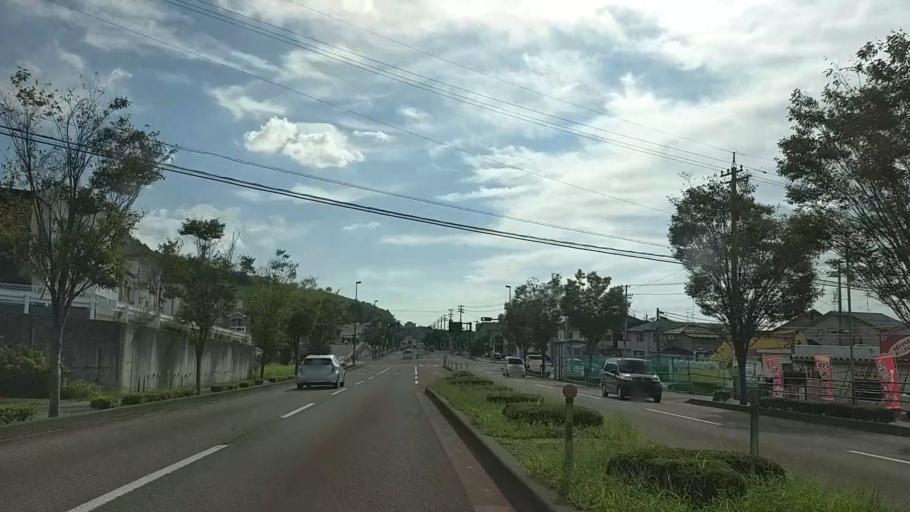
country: JP
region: Ishikawa
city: Nonoichi
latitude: 36.5248
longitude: 136.6433
